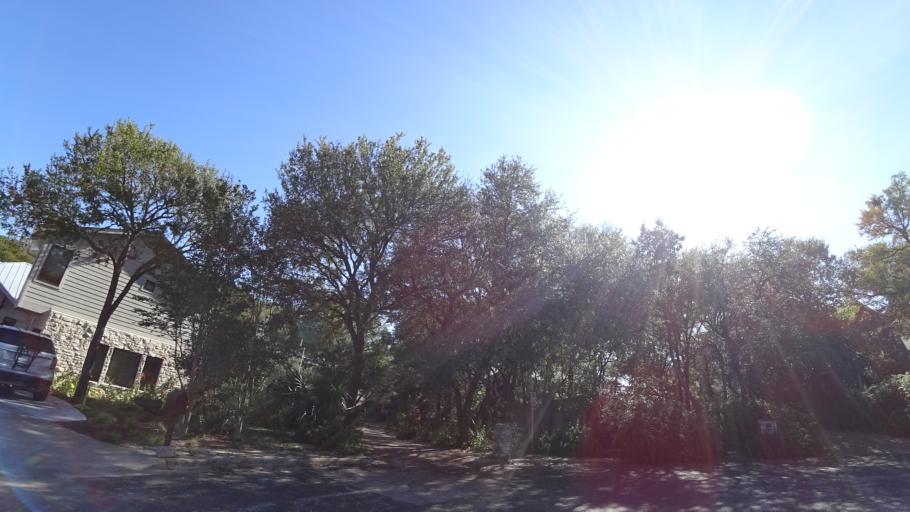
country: US
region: Texas
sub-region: Travis County
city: Rollingwood
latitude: 30.2588
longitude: -97.7858
